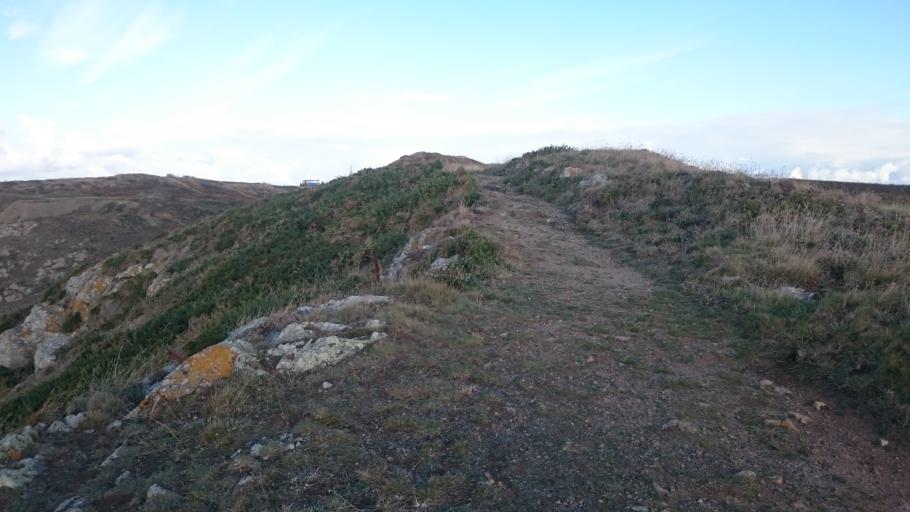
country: GG
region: St Peter Port
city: Saint Peter Port
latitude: 49.4254
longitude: -2.6641
